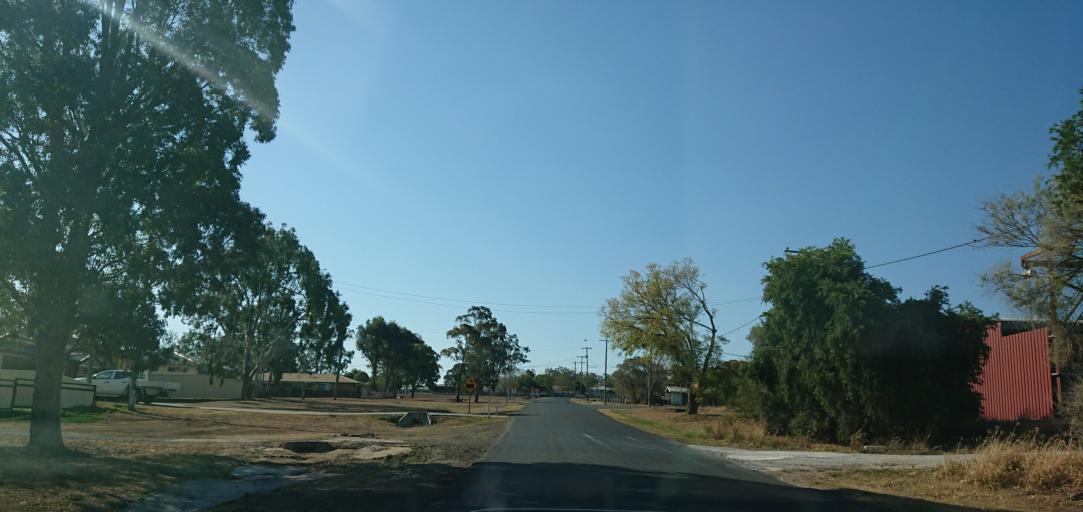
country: AU
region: Queensland
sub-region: Toowoomba
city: Westbrook
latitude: -27.6806
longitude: 151.7131
